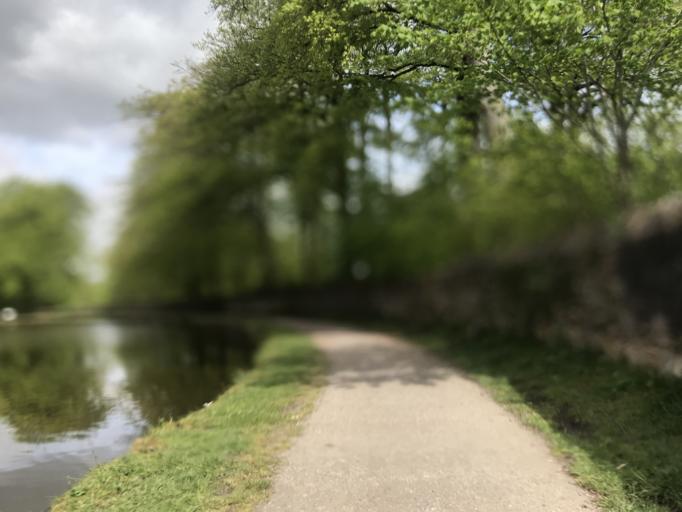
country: GB
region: England
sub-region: Borough of Stockport
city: Marple
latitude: 53.3990
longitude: -2.0583
